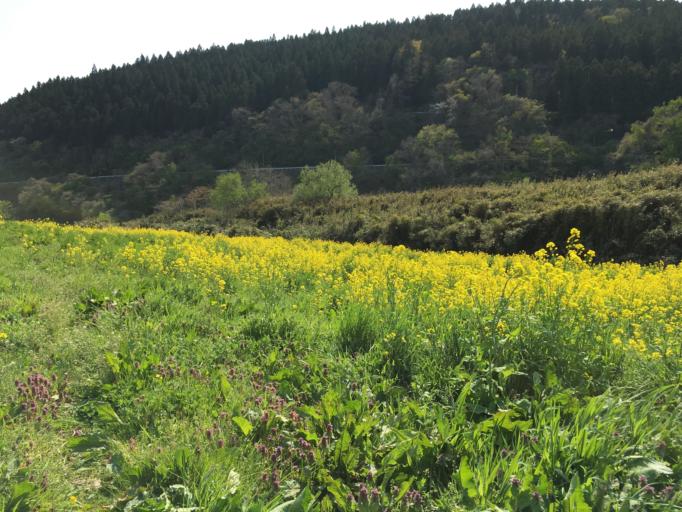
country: JP
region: Iwate
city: Ichinoseki
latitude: 38.8257
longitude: 141.2522
